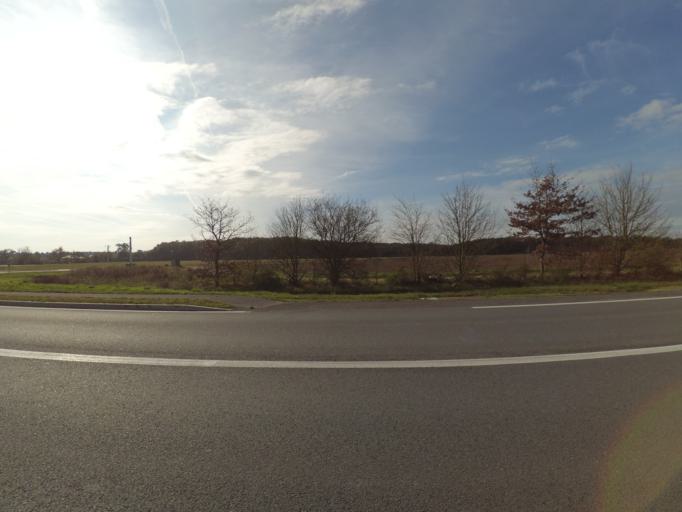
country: FR
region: Pays de la Loire
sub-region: Departement de la Vendee
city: Saint-Hilaire-de-Loulay
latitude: 47.0182
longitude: -1.3438
